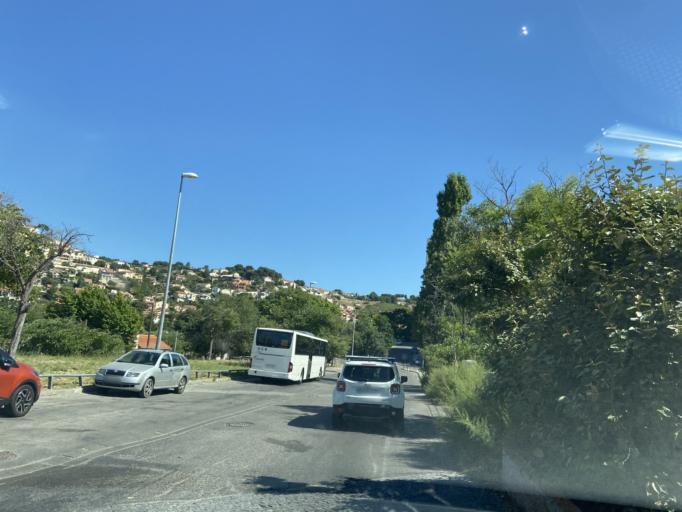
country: FR
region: Provence-Alpes-Cote d'Azur
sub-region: Departement des Bouches-du-Rhone
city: Marseille 15
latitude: 43.3675
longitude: 5.3459
